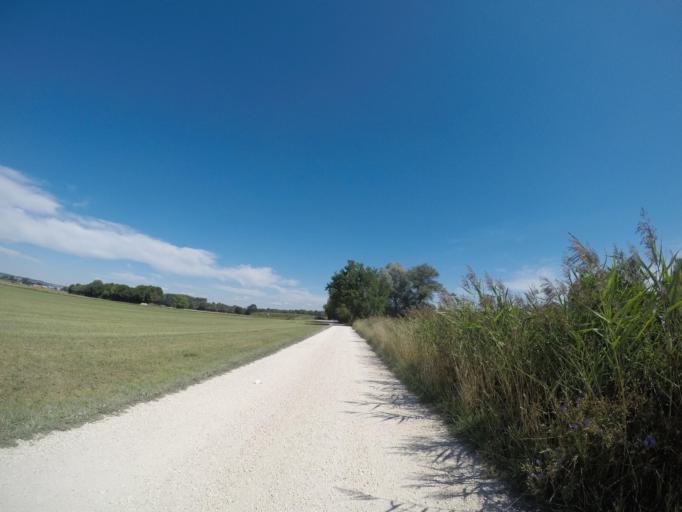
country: DE
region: Bavaria
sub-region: Swabia
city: Senden
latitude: 48.3651
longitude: 10.0578
